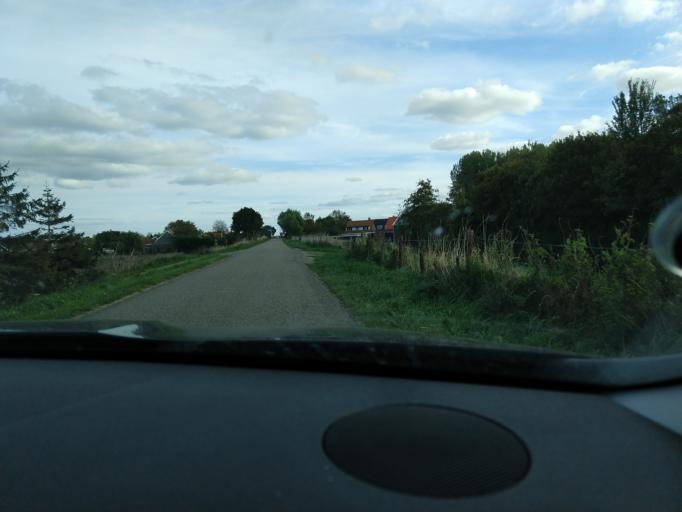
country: NL
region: Zeeland
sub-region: Gemeente Noord-Beveland
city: Kamperland
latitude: 51.5702
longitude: 3.6934
